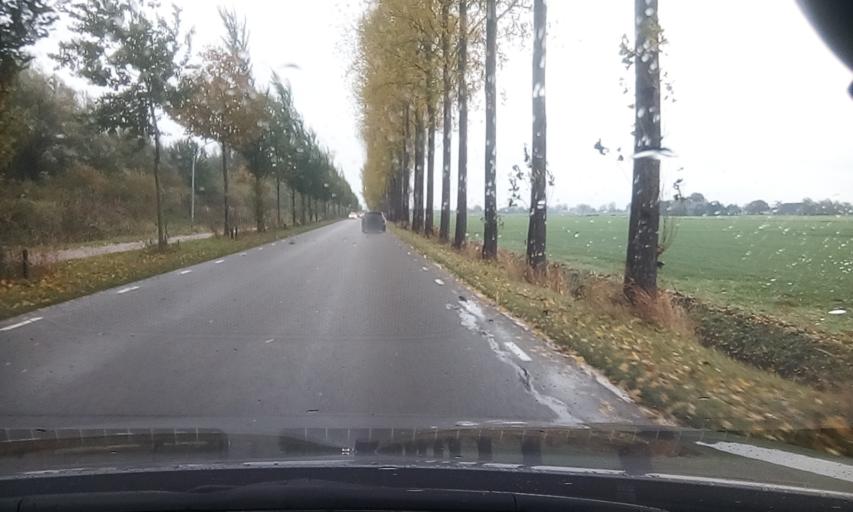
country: NL
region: Groningen
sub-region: Gemeente Groningen
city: Oosterpark
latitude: 53.2276
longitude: 6.6236
